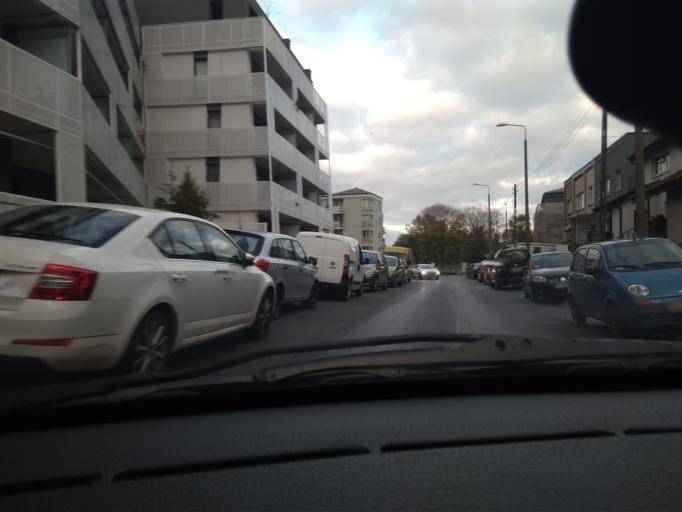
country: PL
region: Greater Poland Voivodeship
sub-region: Poznan
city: Poznan
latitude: 52.4276
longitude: 16.9250
